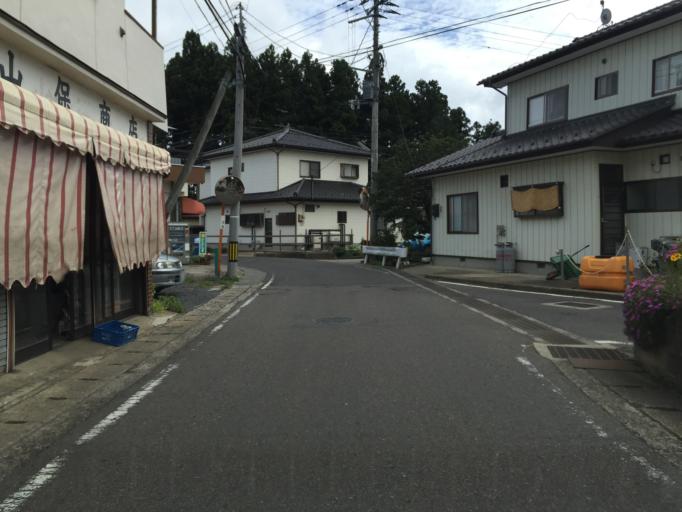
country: JP
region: Fukushima
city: Motomiya
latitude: 37.5330
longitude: 140.3644
